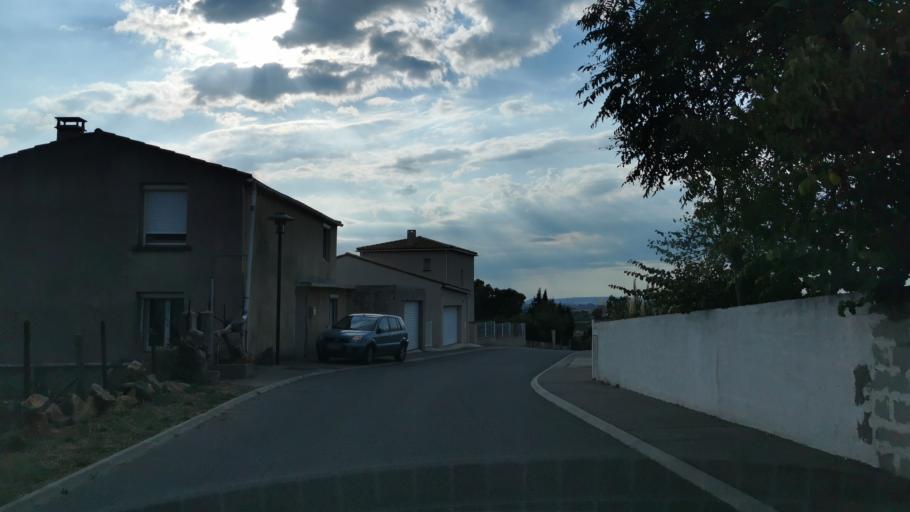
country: FR
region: Languedoc-Roussillon
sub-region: Departement de l'Aude
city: Bizanet
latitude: 43.1636
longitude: 2.8742
